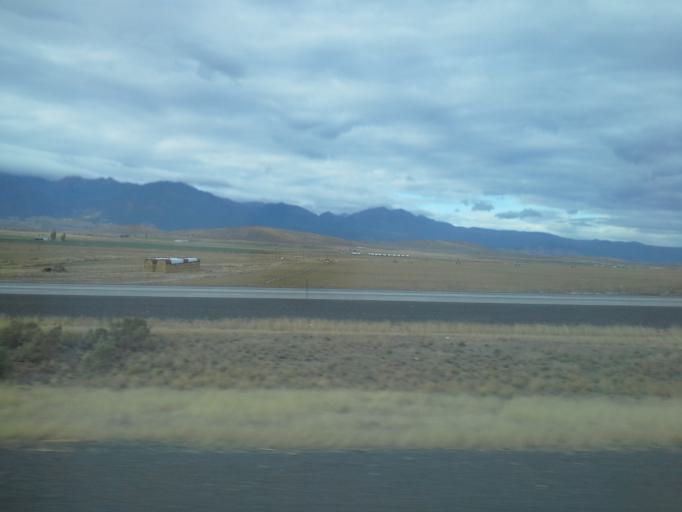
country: US
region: Oregon
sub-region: Baker County
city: Baker City
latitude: 44.9115
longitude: -117.8195
